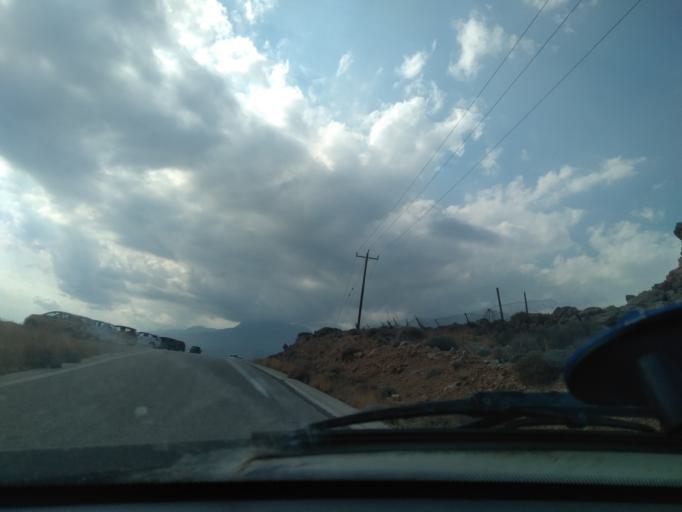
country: GR
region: Crete
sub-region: Nomos Lasithiou
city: Makry-Gialos
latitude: 35.0216
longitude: 26.0177
